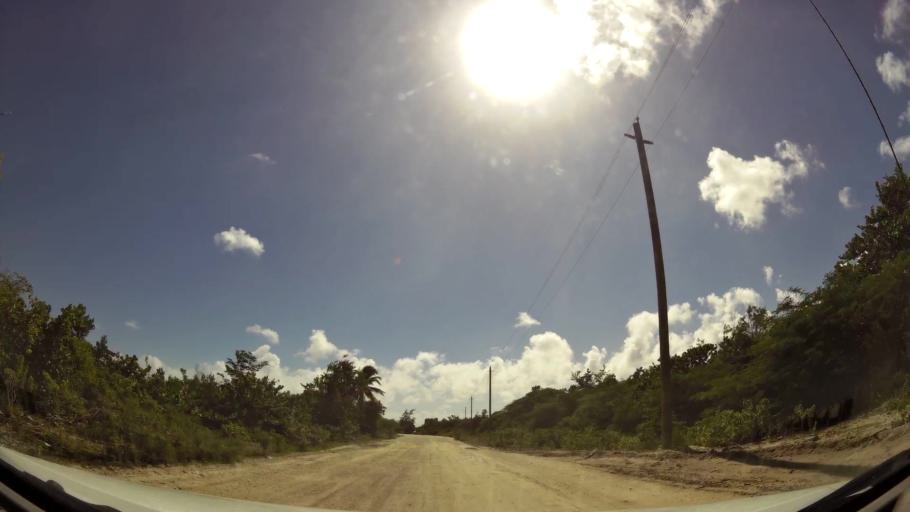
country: AG
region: Barbuda
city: Codrington
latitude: 17.5976
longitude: -61.8293
